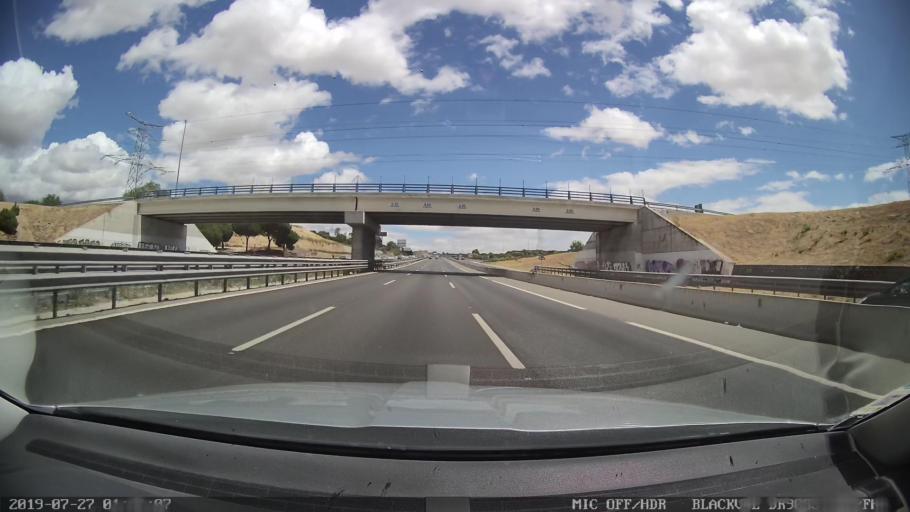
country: ES
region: Madrid
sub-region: Provincia de Madrid
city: Arroyomolinos
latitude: 40.3028
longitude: -3.9218
